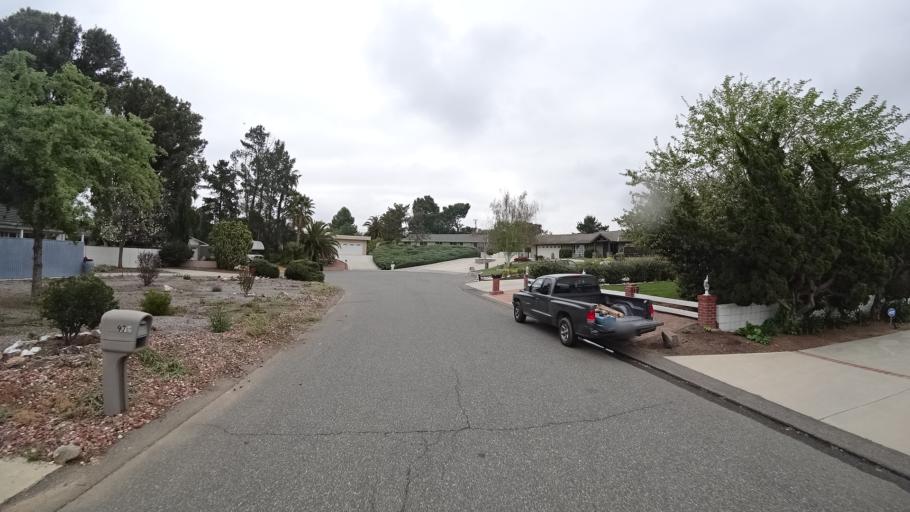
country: US
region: California
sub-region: Ventura County
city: Thousand Oaks
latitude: 34.2023
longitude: -118.8615
